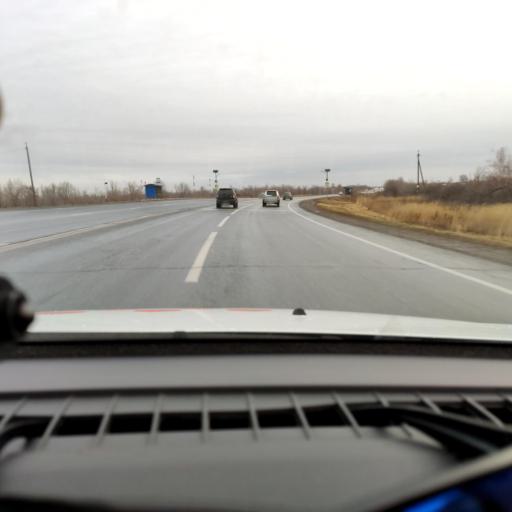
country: RU
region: Samara
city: Novokuybyshevsk
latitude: 53.0718
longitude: 50.0286
